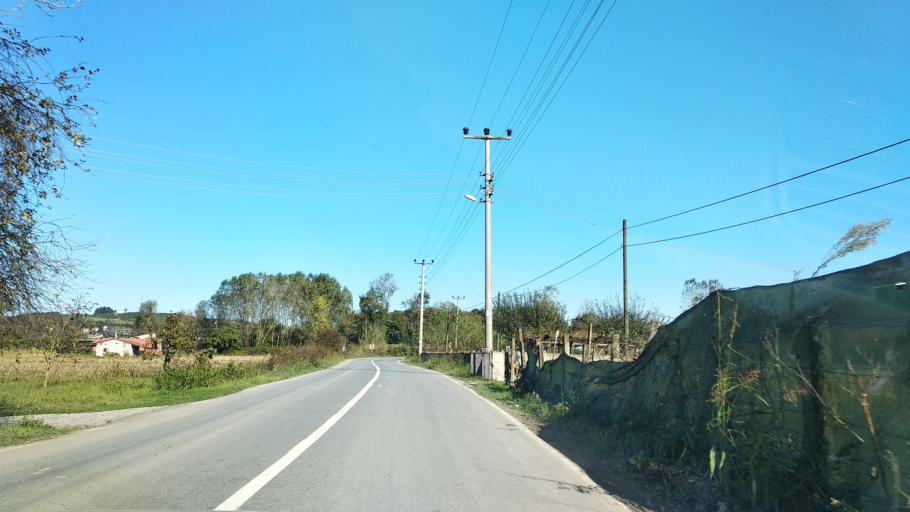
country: TR
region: Sakarya
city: Ortakoy
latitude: 41.0259
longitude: 30.6057
